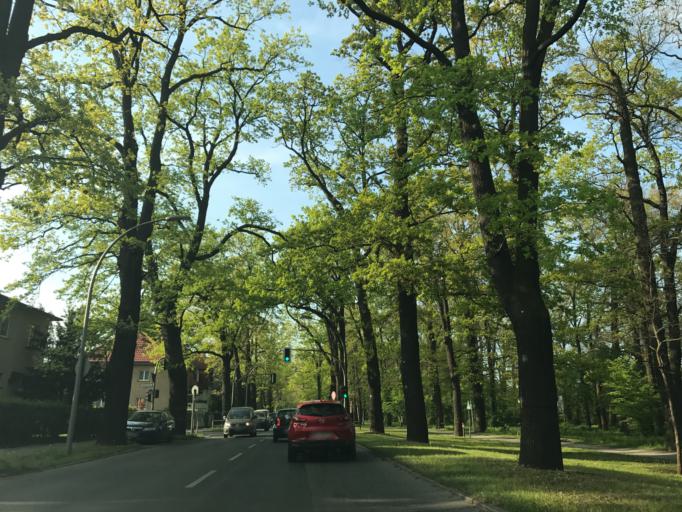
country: DE
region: Berlin
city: Spandau
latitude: 52.5578
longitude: 13.1981
